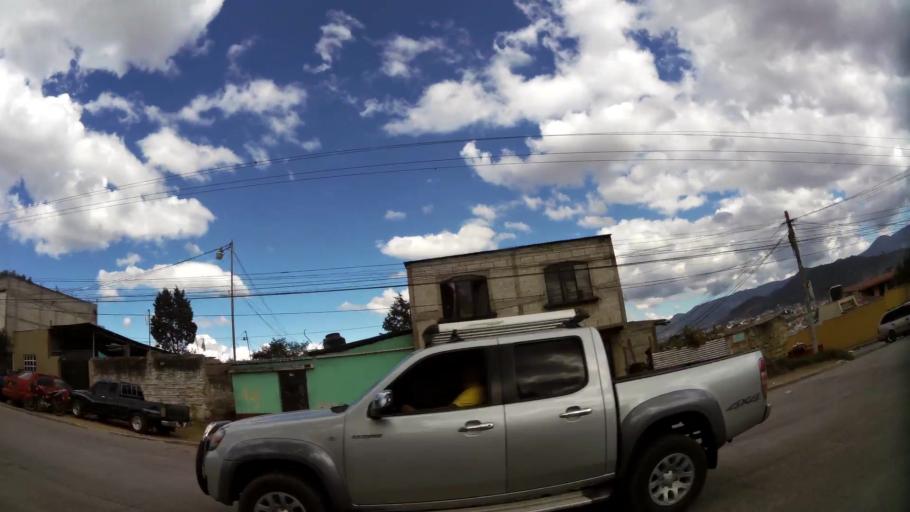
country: GT
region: Quetzaltenango
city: Quetzaltenango
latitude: 14.8423
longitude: -91.5357
